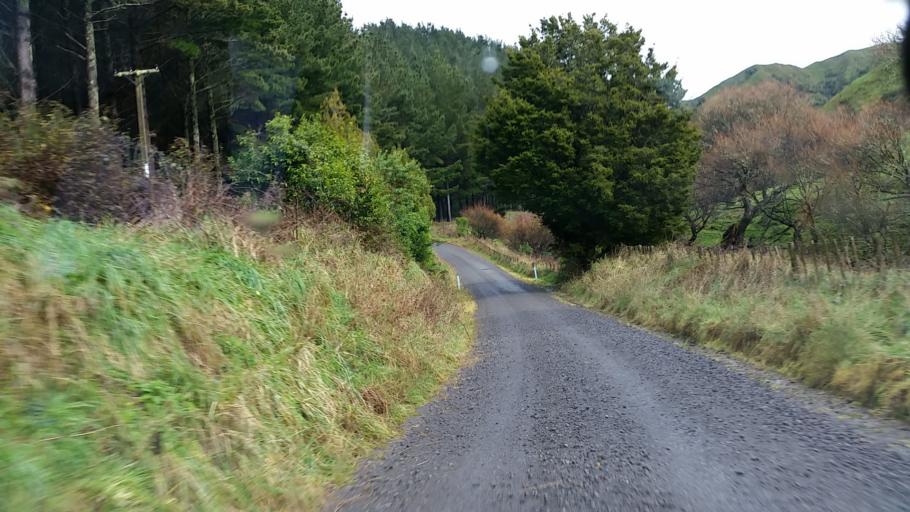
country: NZ
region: Taranaki
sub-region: South Taranaki District
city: Eltham
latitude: -39.5027
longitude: 174.4110
